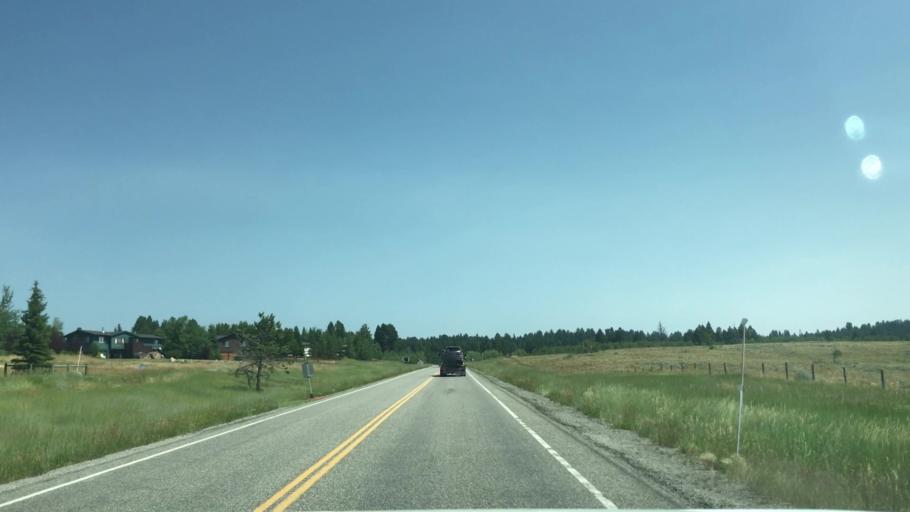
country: US
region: Montana
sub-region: Gallatin County
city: West Yellowstone
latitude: 44.7917
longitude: -111.1092
